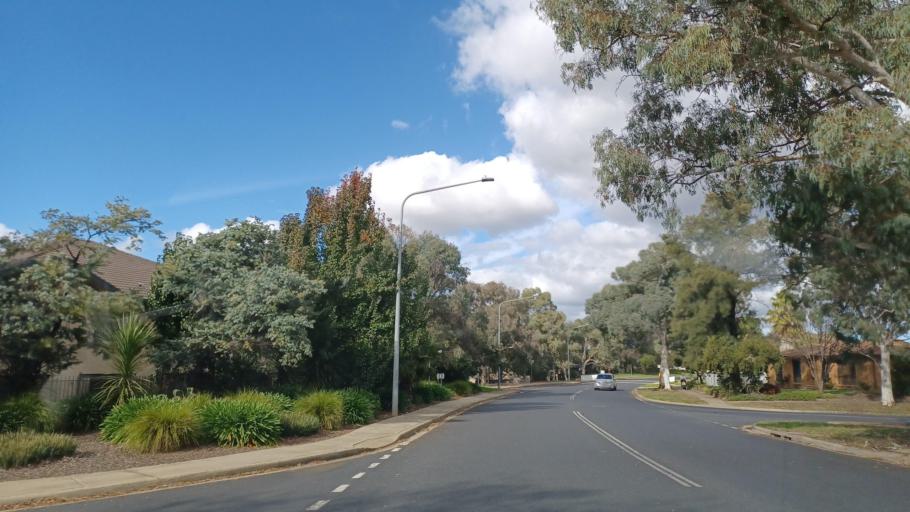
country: AU
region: Australian Capital Territory
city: Belconnen
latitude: -35.2085
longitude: 149.0724
